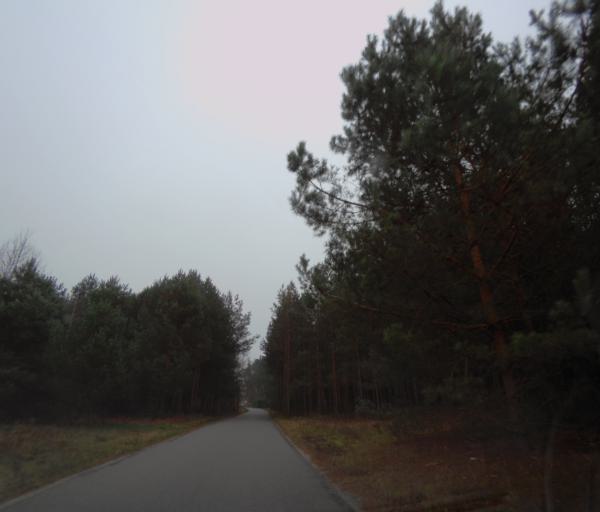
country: PL
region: Subcarpathian Voivodeship
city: Nowa Sarzyna
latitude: 50.2984
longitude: 22.3494
